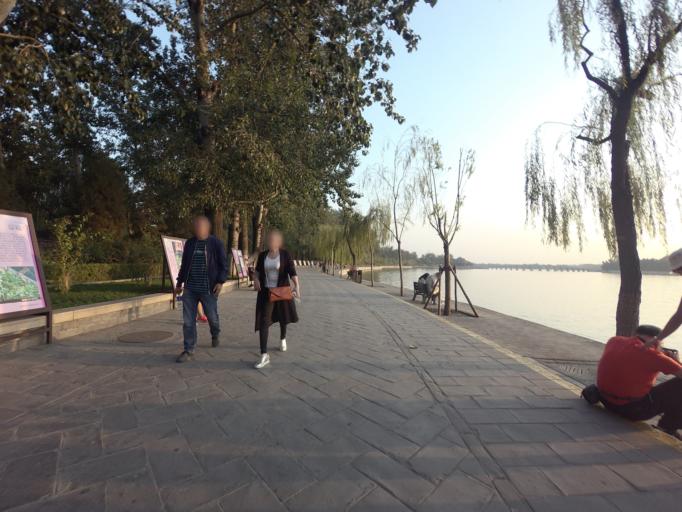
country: CN
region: Beijing
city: Haidian
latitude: 39.9935
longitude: 116.2743
